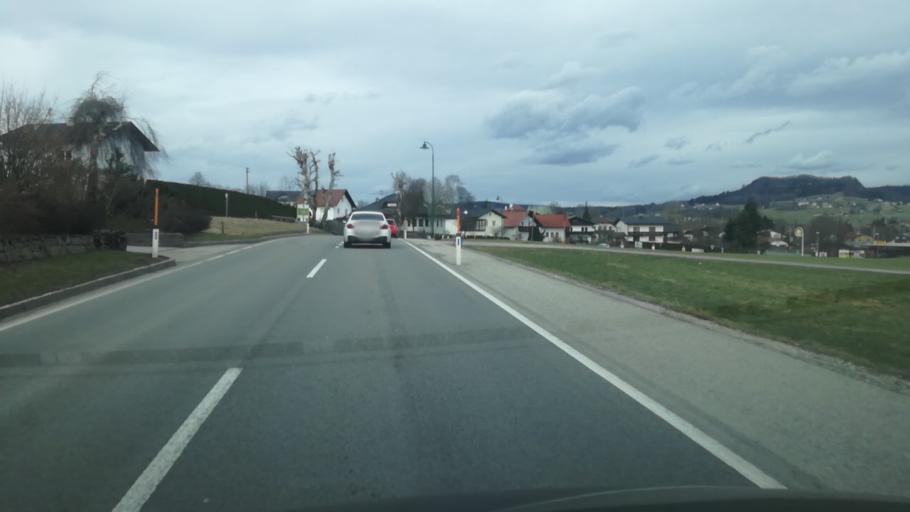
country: AT
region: Upper Austria
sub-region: Politischer Bezirk Vocklabruck
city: Frankenburg
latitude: 48.0611
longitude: 13.4805
